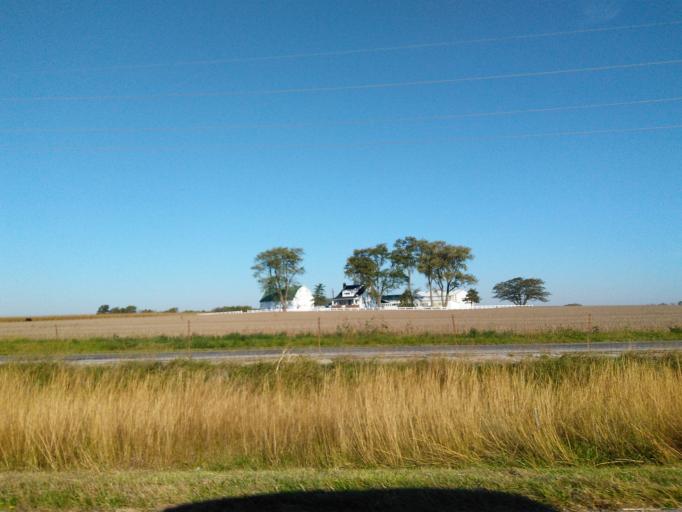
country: US
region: Illinois
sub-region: Madison County
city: Highland
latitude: 38.8178
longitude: -89.5636
